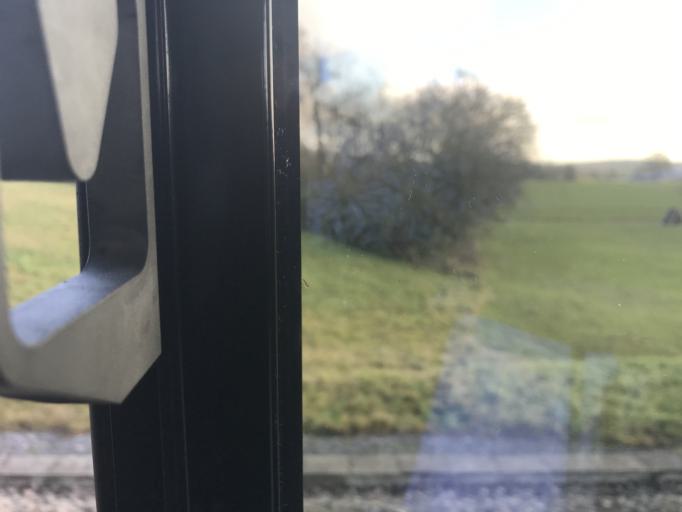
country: CH
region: Zurich
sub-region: Bezirk Andelfingen
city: Dachsen
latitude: 47.6654
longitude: 8.5977
